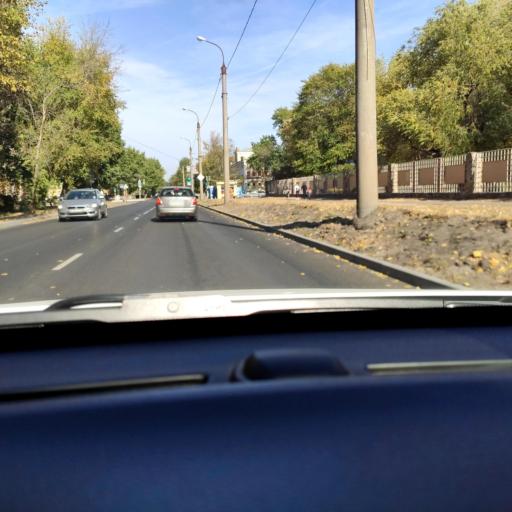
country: RU
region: Voronezj
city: Voronezh
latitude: 51.6416
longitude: 39.2407
